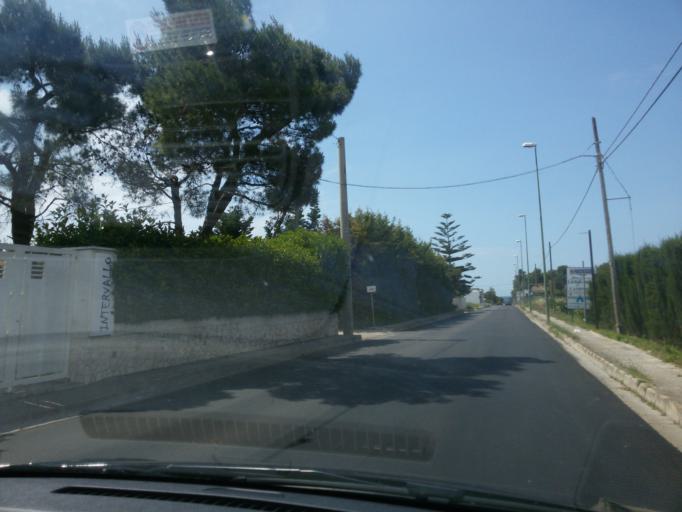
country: IT
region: Apulia
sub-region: Provincia di Lecce
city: Porto Cesareo
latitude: 40.2934
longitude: 17.8544
